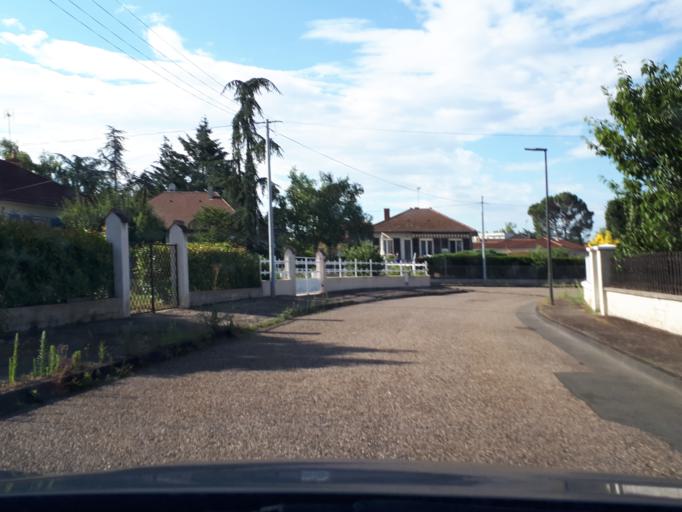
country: FR
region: Rhone-Alpes
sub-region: Departement de la Loire
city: Feurs
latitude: 45.7315
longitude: 4.2267
